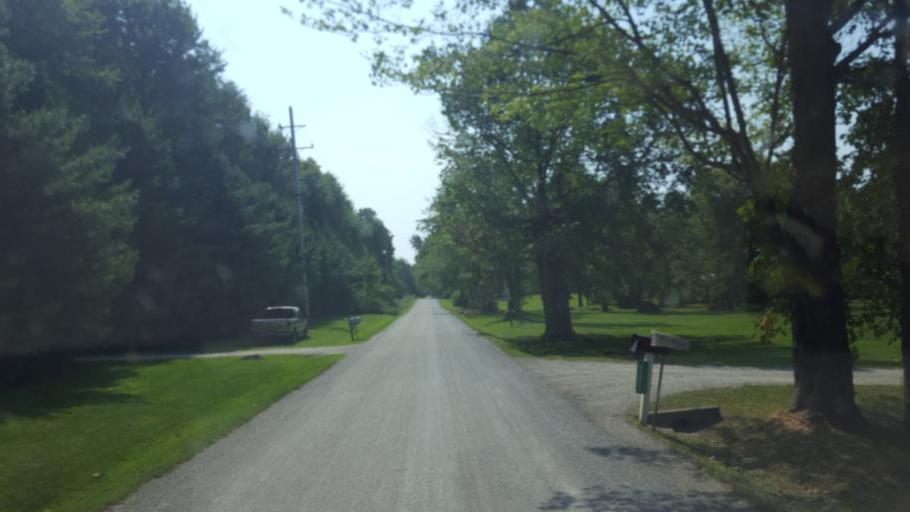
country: US
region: Ohio
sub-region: Ashtabula County
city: Orwell
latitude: 41.5247
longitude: -80.8846
